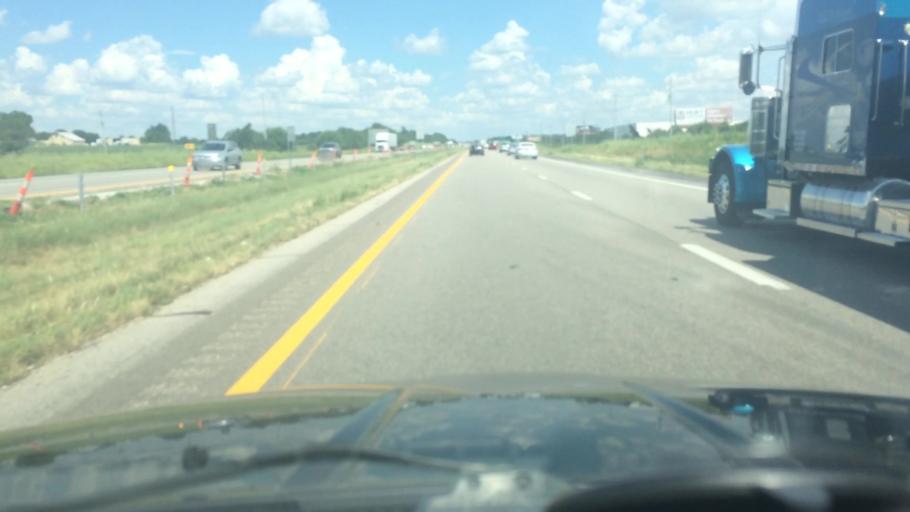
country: US
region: Missouri
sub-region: Greene County
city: Springfield
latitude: 37.2502
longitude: -93.2143
